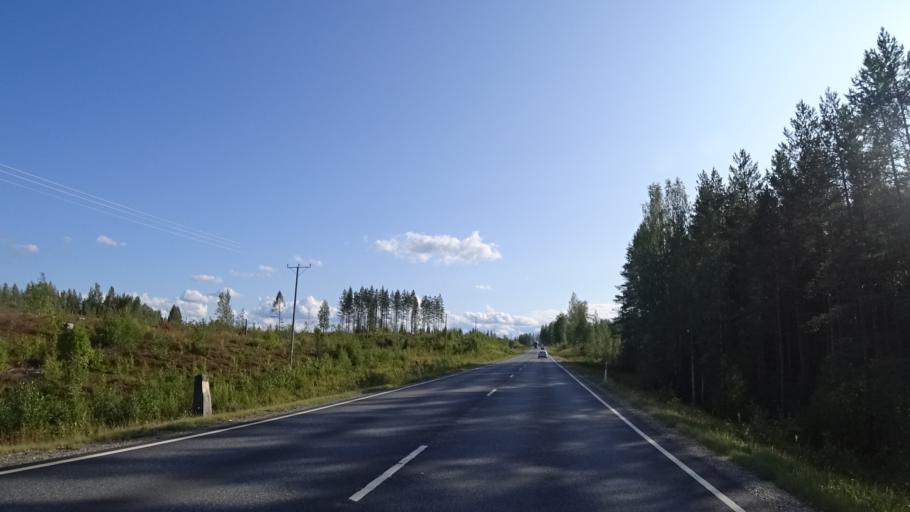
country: FI
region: North Karelia
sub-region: Keski-Karjala
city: Kesaelahti
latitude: 62.0260
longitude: 29.8950
